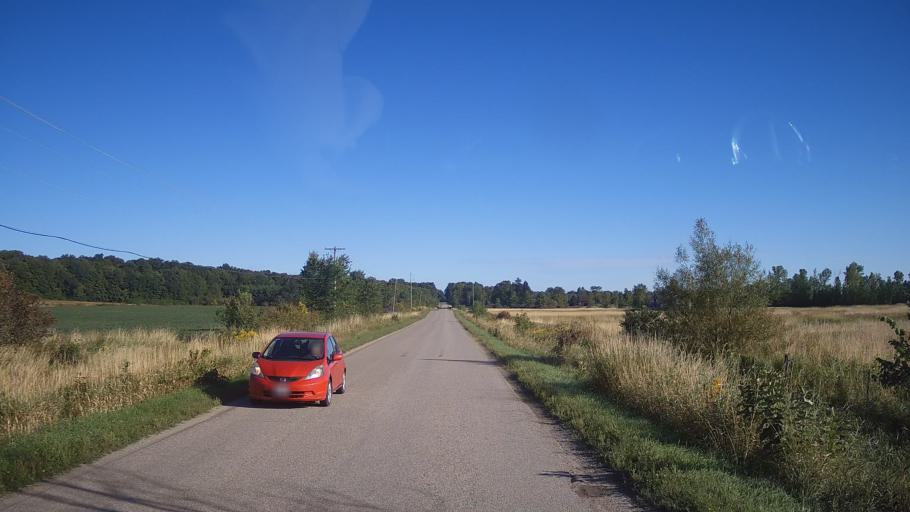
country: US
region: New York
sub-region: Jefferson County
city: Alexandria Bay
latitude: 44.4352
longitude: -75.9818
